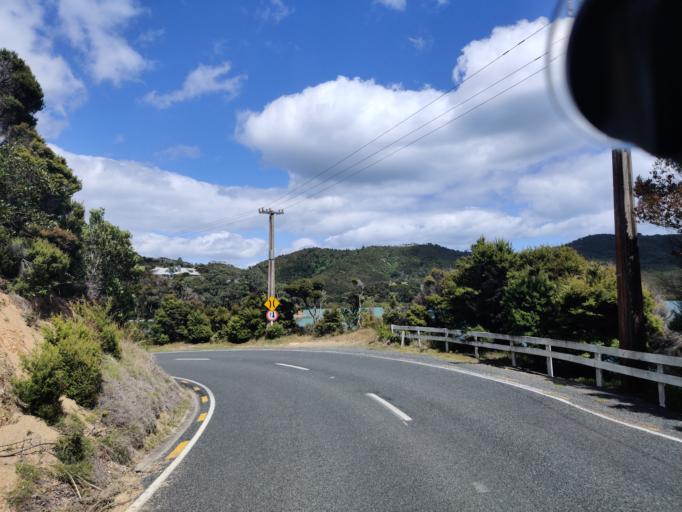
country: NZ
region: Northland
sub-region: Far North District
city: Paihia
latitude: -35.2586
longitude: 174.2318
